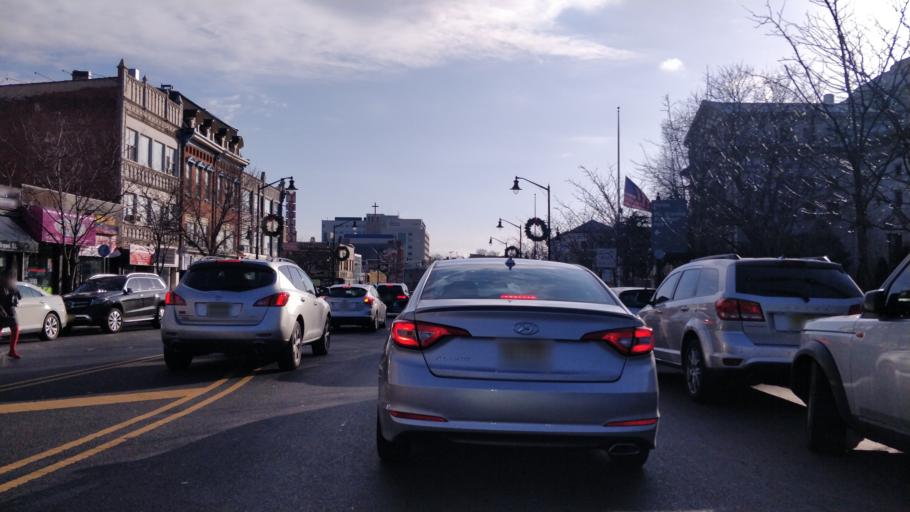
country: US
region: New Jersey
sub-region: Union County
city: Elizabeth
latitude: 40.6629
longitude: -74.2151
